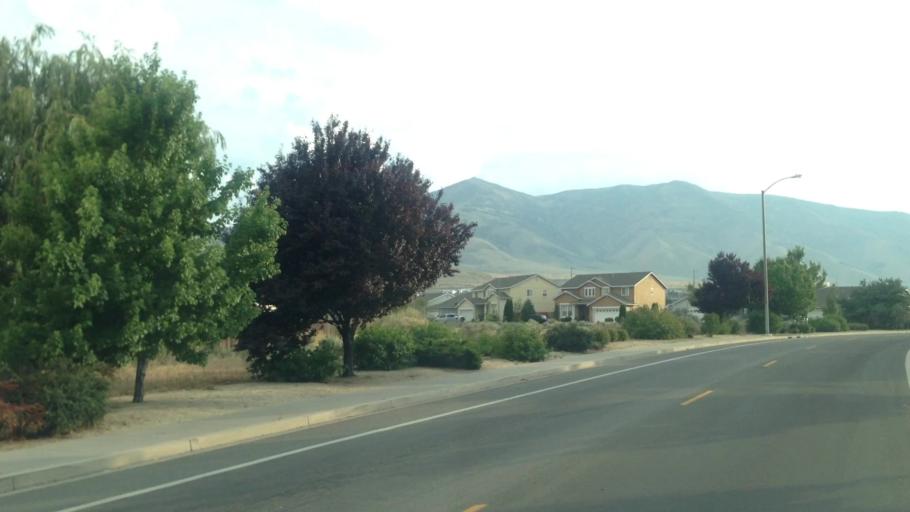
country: US
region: Nevada
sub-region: Washoe County
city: Lemmon Valley
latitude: 39.6257
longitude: -119.8759
